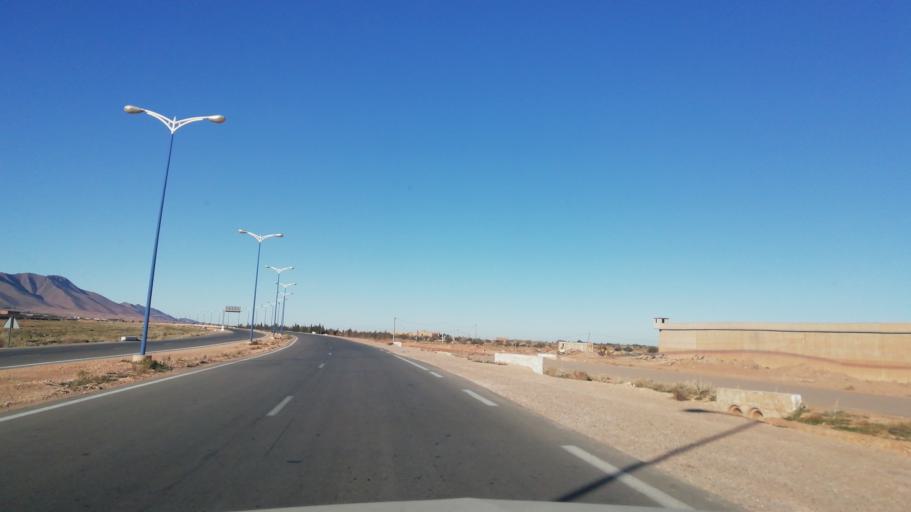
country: DZ
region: Wilaya de Naama
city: Naama
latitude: 33.5585
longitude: -0.2369
